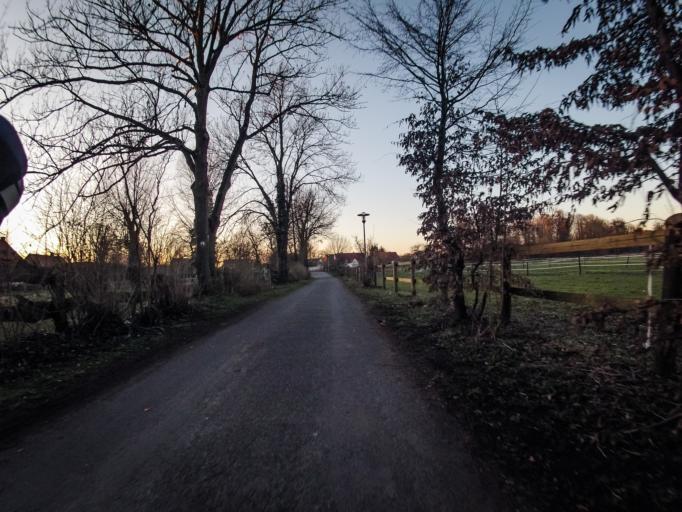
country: DE
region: North Rhine-Westphalia
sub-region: Regierungsbezirk Munster
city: Lotte
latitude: 52.3104
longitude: 7.9391
